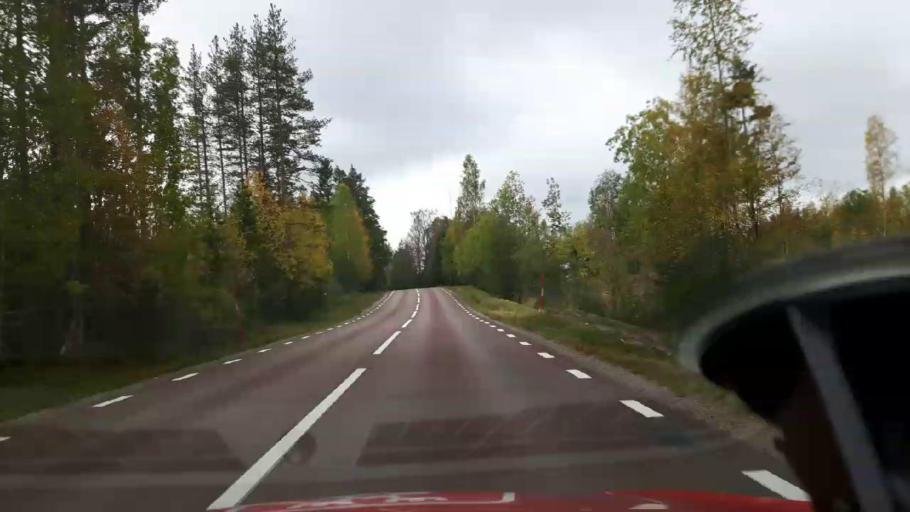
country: SE
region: Jaemtland
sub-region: Harjedalens Kommun
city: Sveg
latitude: 62.2007
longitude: 14.8528
